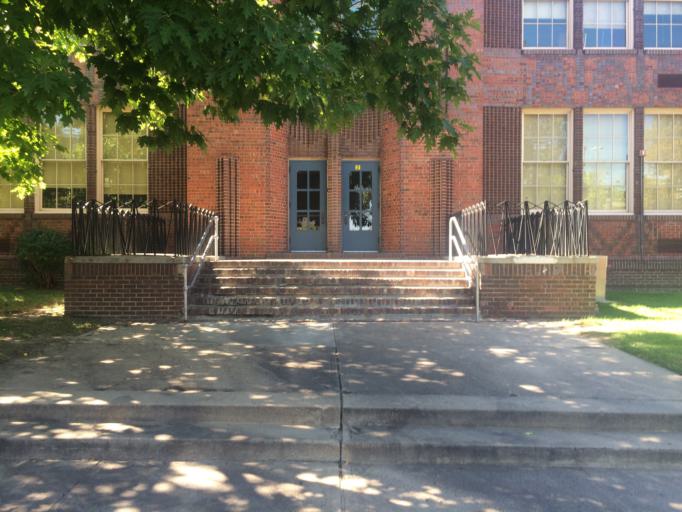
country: US
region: Colorado
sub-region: Denver County
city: Denver
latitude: 39.7672
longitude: -105.0081
